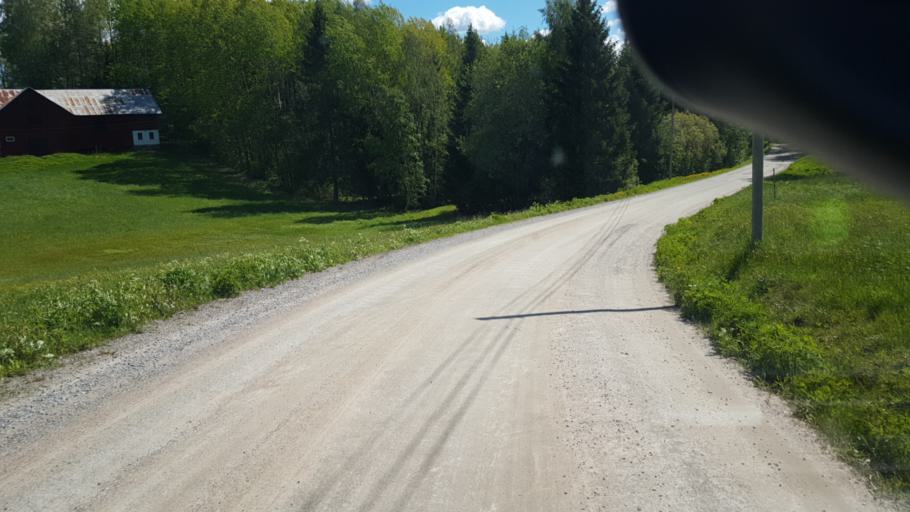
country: SE
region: Vaermland
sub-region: Sunne Kommun
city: Sunne
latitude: 59.6890
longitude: 12.8910
